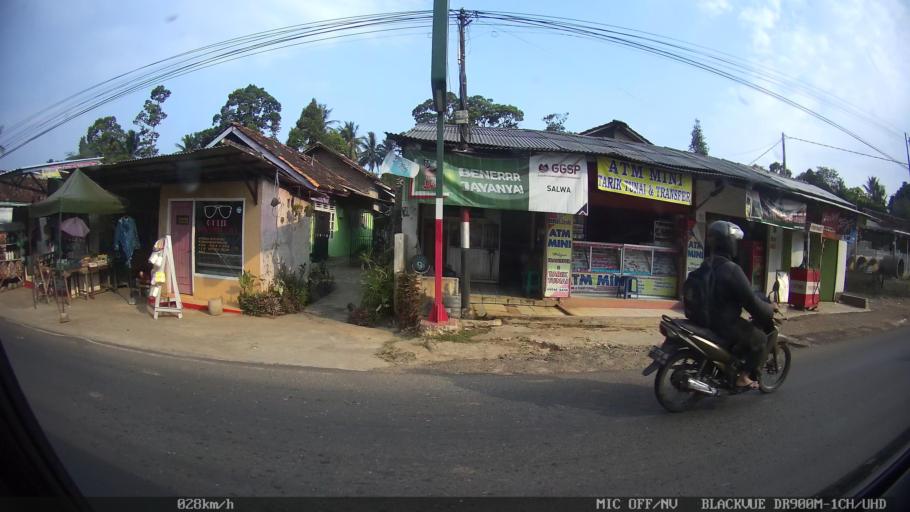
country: ID
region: Lampung
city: Natar
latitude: -5.3684
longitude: 105.1774
